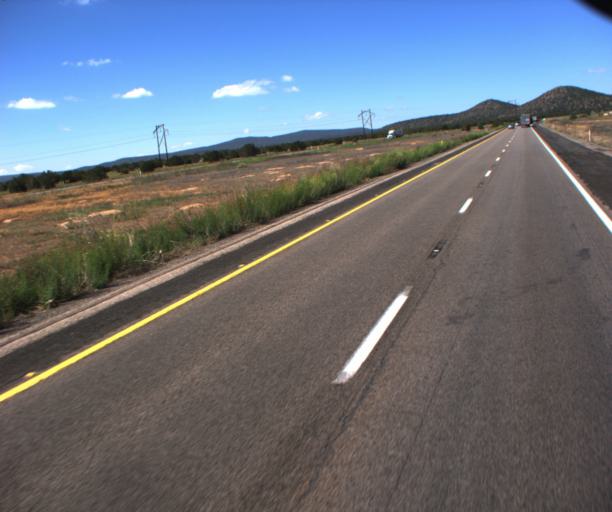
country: US
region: Arizona
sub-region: Mohave County
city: Peach Springs
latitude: 35.3057
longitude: -112.9933
